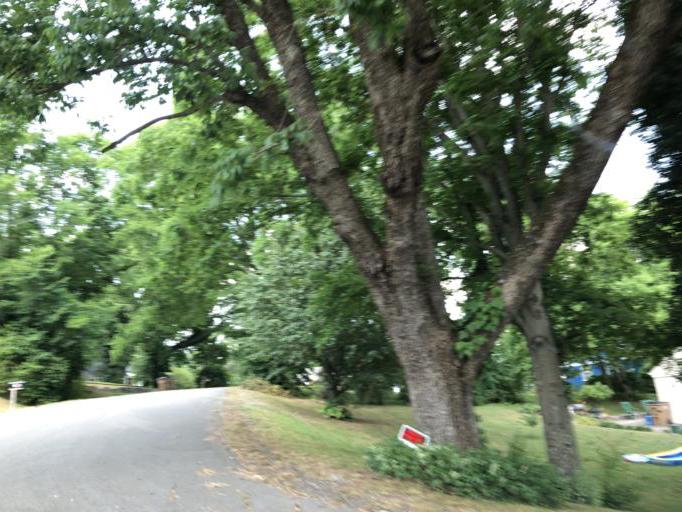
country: US
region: Tennessee
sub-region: Davidson County
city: Goodlettsville
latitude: 36.2464
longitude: -86.7182
